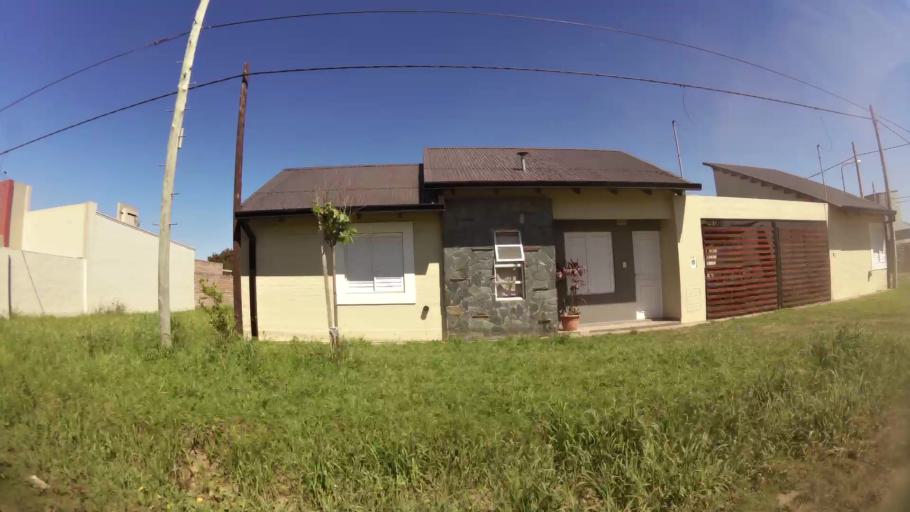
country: AR
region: Santa Fe
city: Esperanza
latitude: -31.4356
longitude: -60.9301
